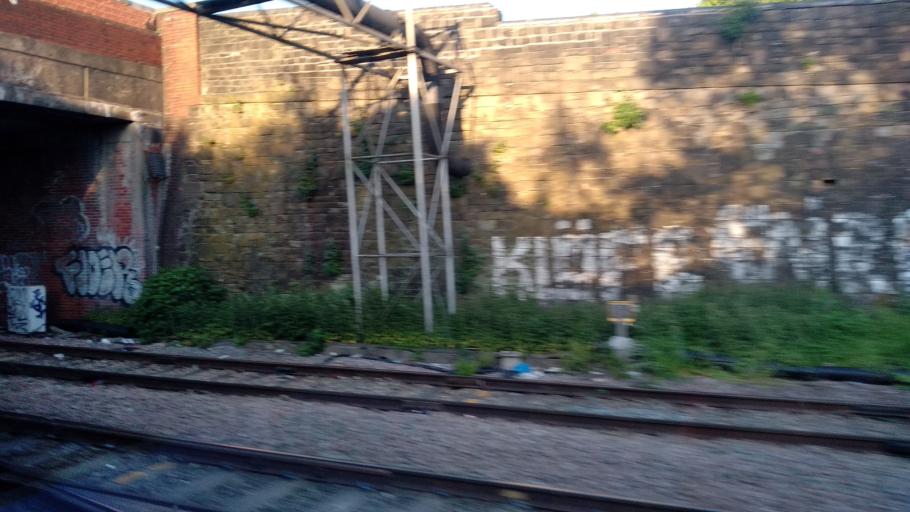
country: GB
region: England
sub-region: Bristol
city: Bristol
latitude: 51.4539
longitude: -2.5674
